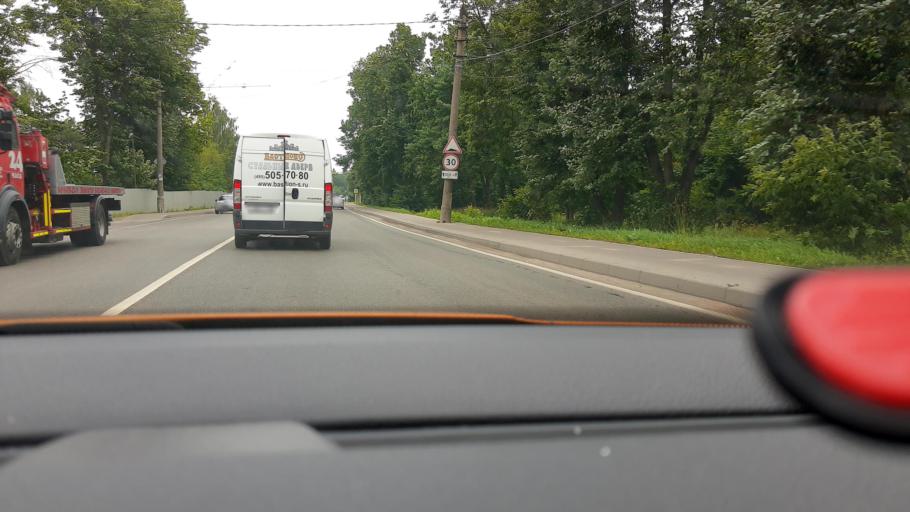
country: RU
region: Moskovskaya
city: Pushkino
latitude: 56.0086
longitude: 37.8732
